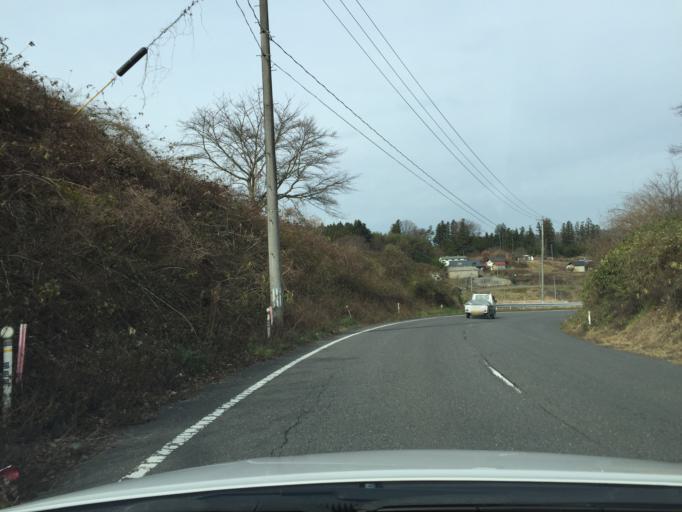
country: JP
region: Fukushima
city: Funehikimachi-funehiki
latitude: 37.4000
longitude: 140.5923
